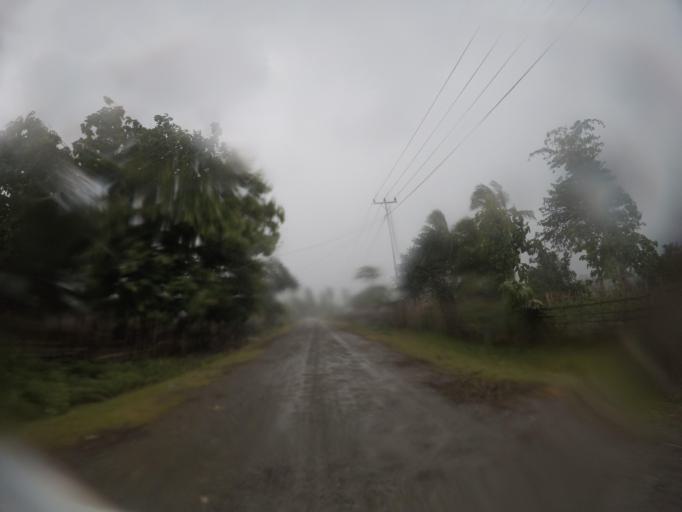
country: TL
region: Bobonaro
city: Maliana
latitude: -8.8558
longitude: 125.0990
